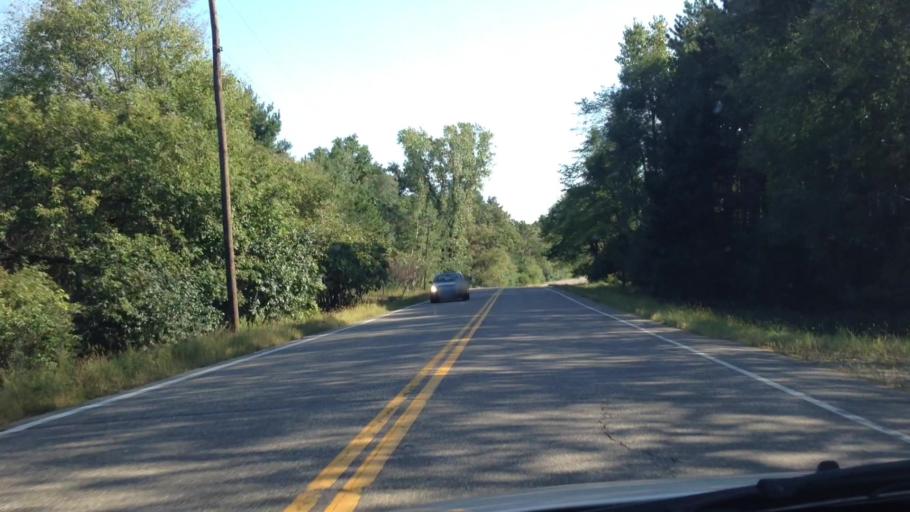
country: US
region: Minnesota
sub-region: Washington County
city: Stillwater
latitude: 45.1185
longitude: -92.8137
